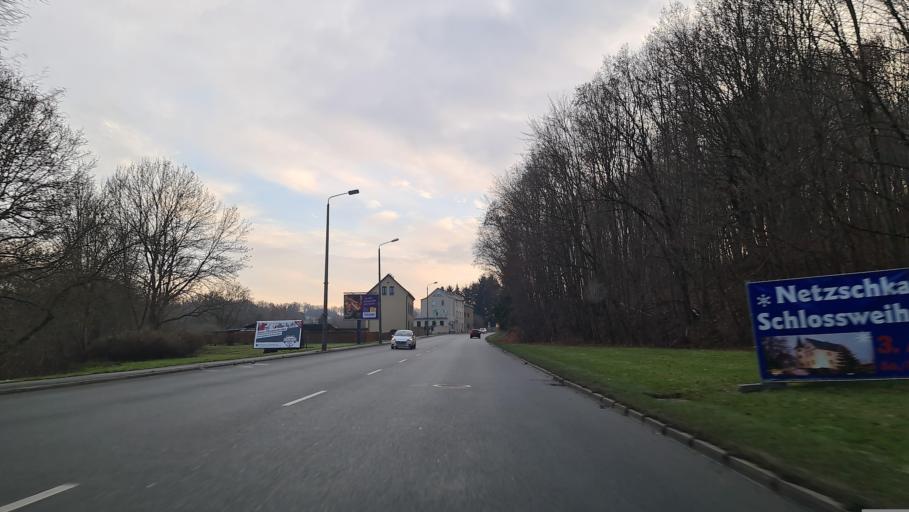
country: DE
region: Saxony
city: Netzschkau
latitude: 50.6169
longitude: 12.2539
